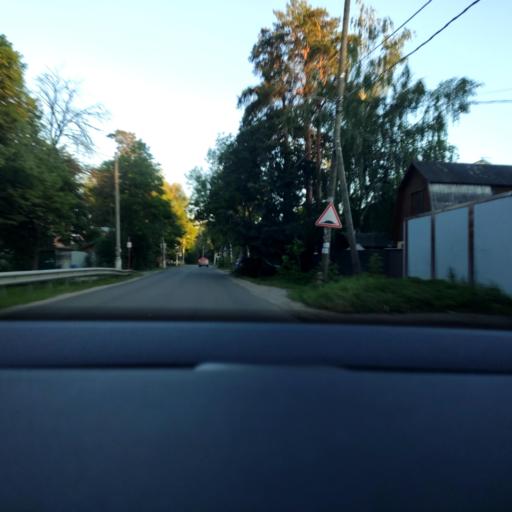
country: RU
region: Moskovskaya
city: Reutov
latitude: 55.7639
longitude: 37.8963
